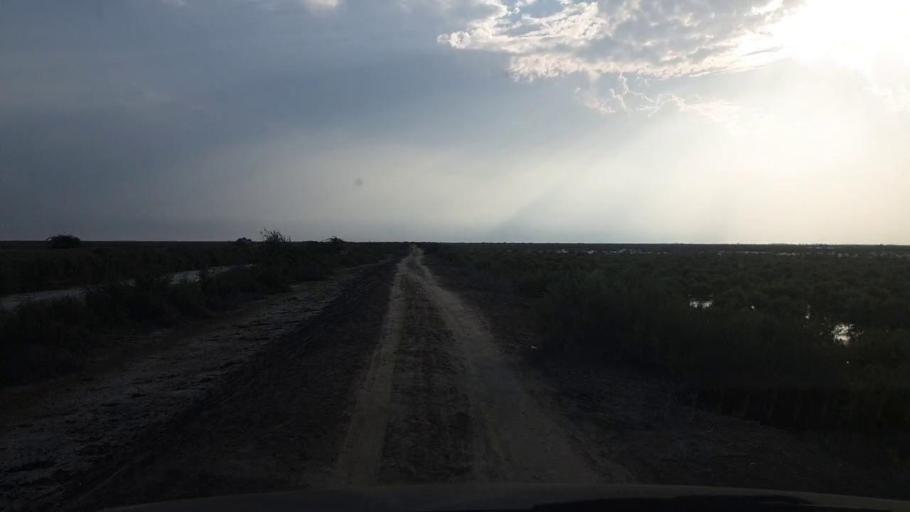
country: PK
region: Sindh
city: Badin
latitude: 24.4368
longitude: 68.6731
